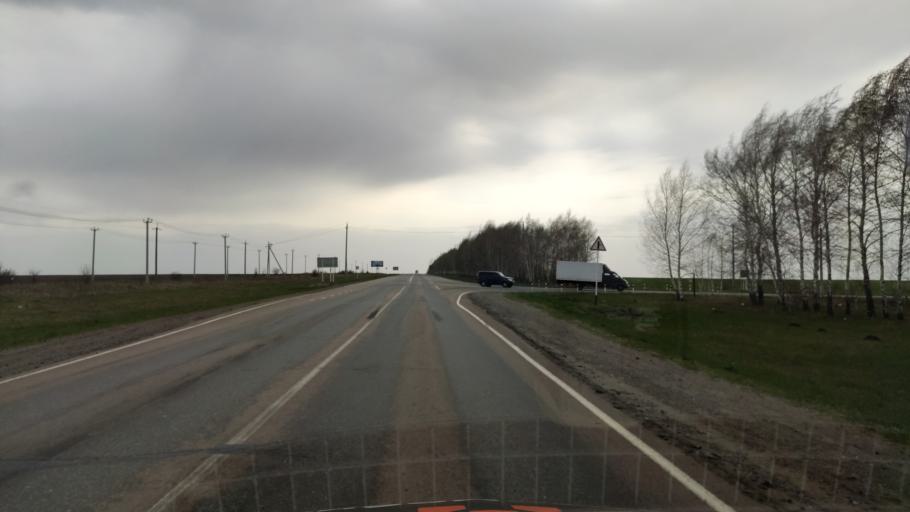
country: RU
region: Kursk
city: Gorshechnoye
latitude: 51.5082
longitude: 37.9977
